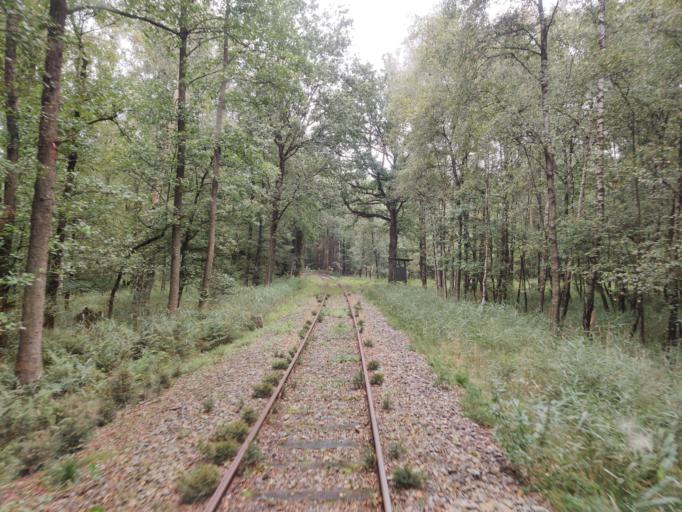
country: DE
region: Lower Saxony
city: Basdahl
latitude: 53.4250
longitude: 9.0179
